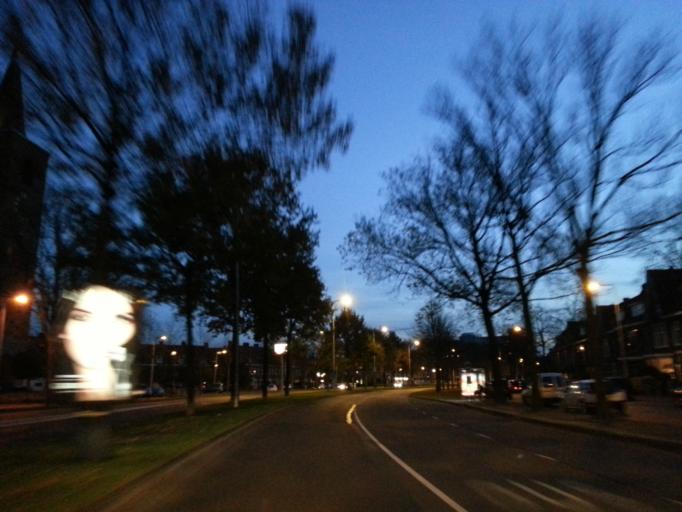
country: NL
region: South Holland
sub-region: Gemeente Leiden
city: Leiden
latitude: 52.1513
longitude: 4.4945
